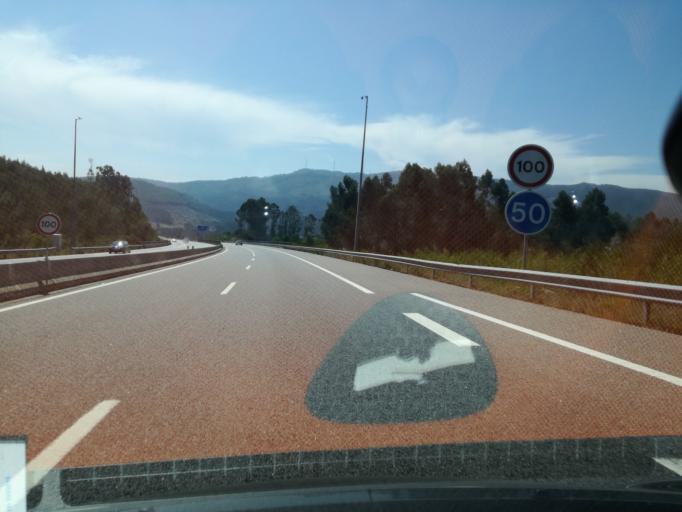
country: PT
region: Viana do Castelo
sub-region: Caminha
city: Vila Praia de Ancora
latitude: 41.8119
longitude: -8.8054
